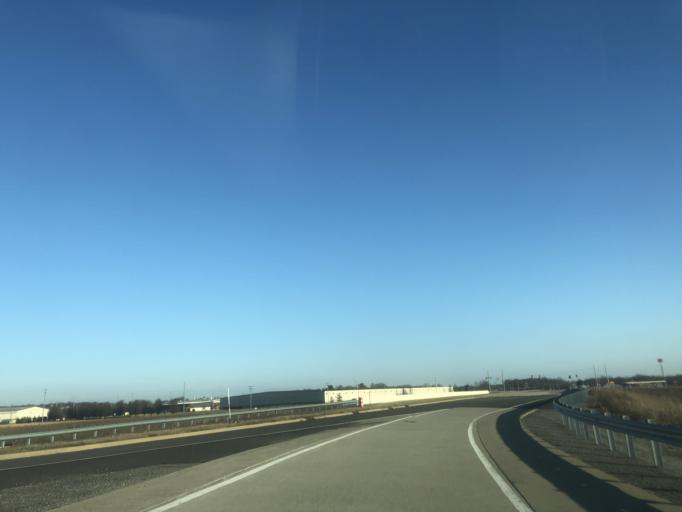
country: US
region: Tennessee
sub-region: Sumner County
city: Portland
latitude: 36.6317
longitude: -86.5754
